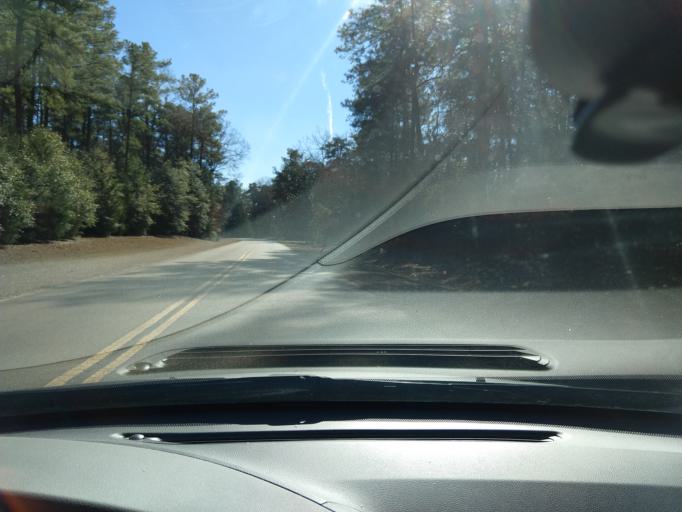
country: US
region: Georgia
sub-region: Macon County
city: Oglethorpe
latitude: 32.2049
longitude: -84.1285
